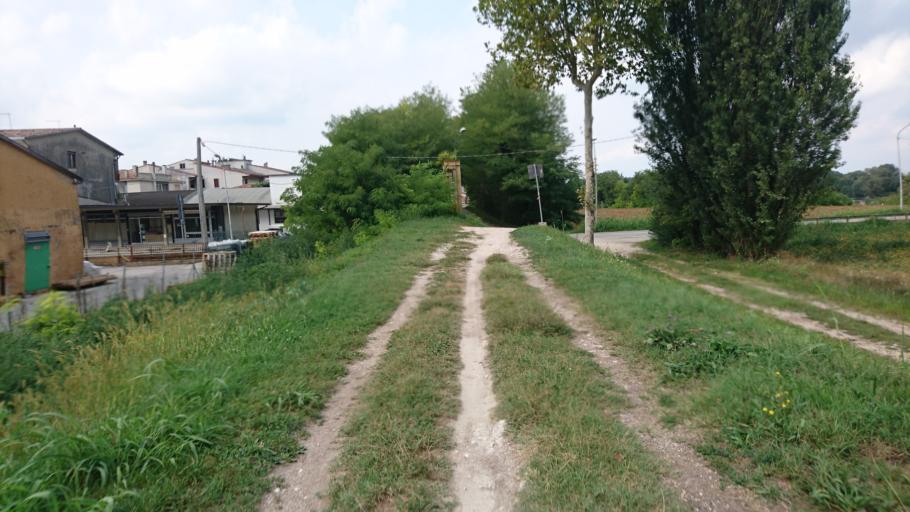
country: IT
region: Veneto
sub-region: Provincia di Padova
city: Limena
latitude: 45.4788
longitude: 11.8469
